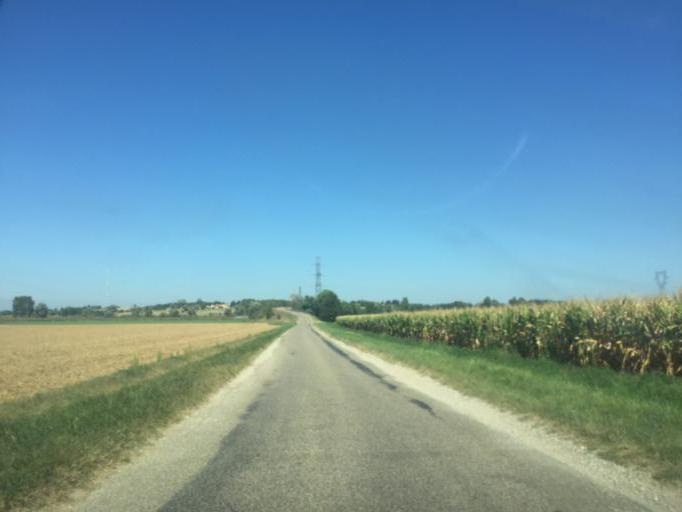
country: FR
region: Rhone-Alpes
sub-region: Departement de l'Ain
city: Saint-Maurice-de-Beynost
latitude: 45.8550
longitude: 4.9748
